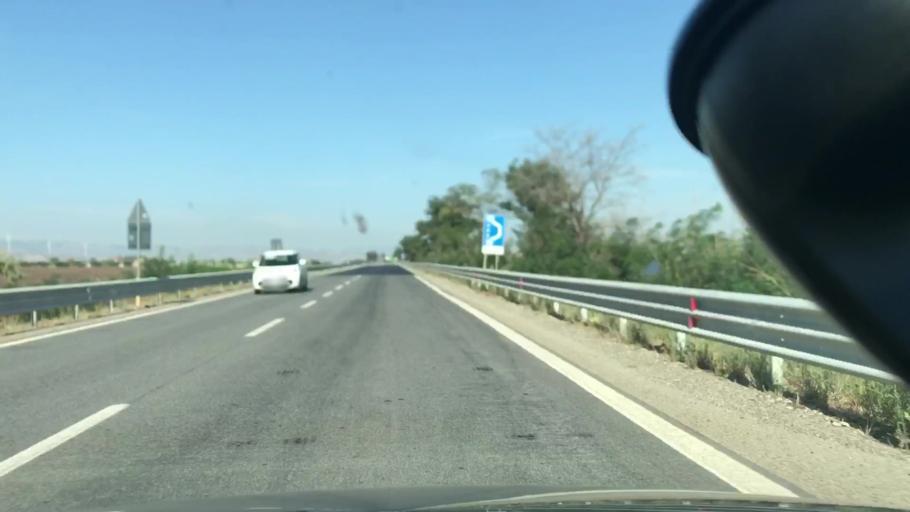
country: IT
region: Basilicate
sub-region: Provincia di Potenza
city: Melfi
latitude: 41.0719
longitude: 15.6520
